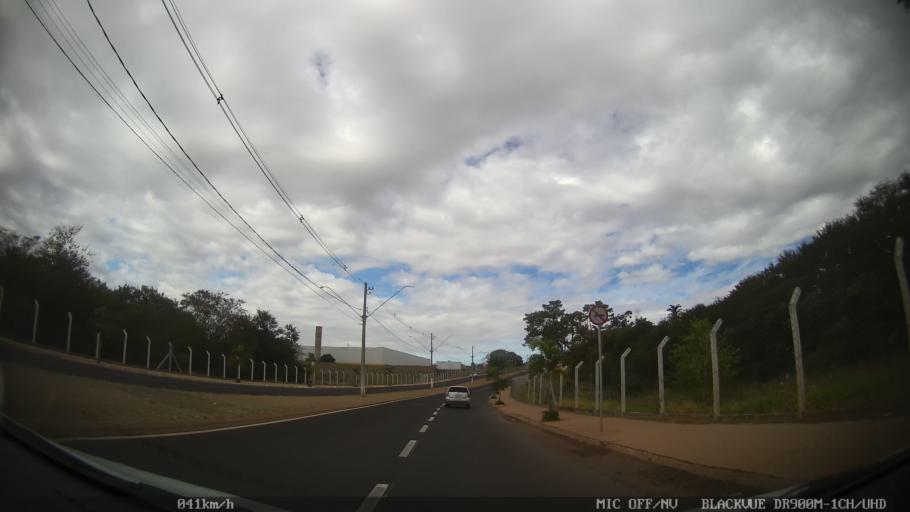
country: BR
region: Sao Paulo
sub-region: Sao Jose Do Rio Preto
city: Sao Jose do Rio Preto
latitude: -20.8151
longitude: -49.4816
